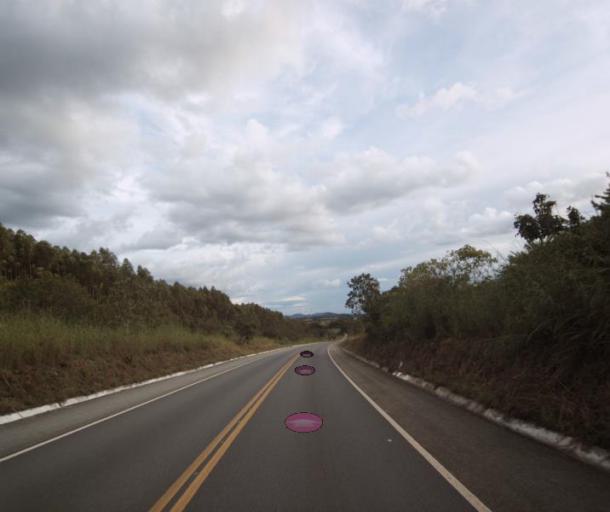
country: BR
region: Goias
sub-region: Barro Alto
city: Barro Alto
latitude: -14.9079
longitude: -48.6452
